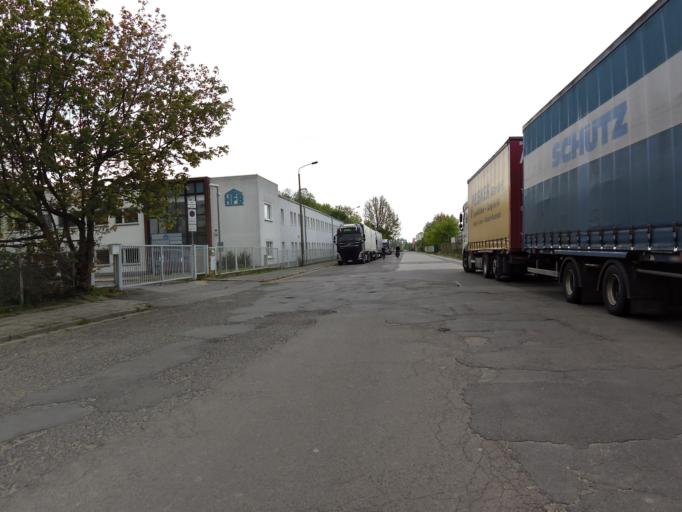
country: DE
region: Saxony
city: Leipzig
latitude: 51.3759
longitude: 12.3949
